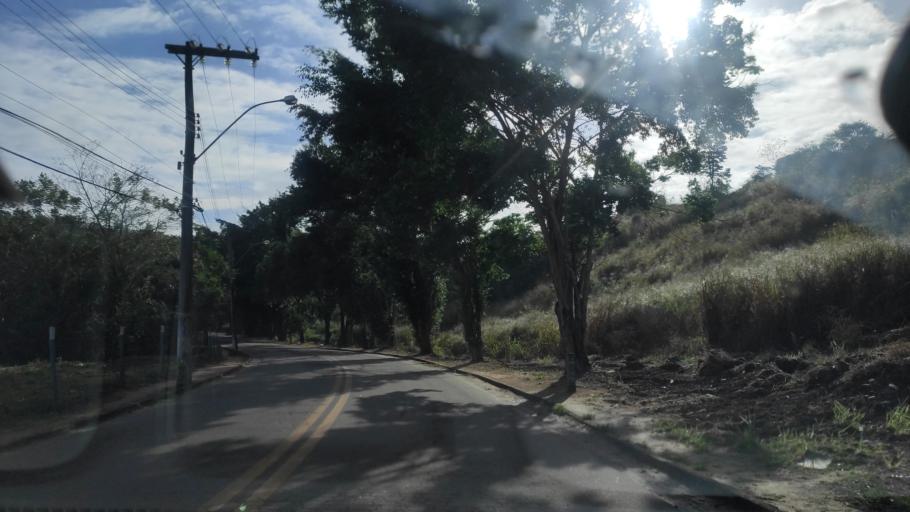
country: BR
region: Espirito Santo
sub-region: Nova Venecia
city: Nova Venecia
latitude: -18.7155
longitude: -40.3861
